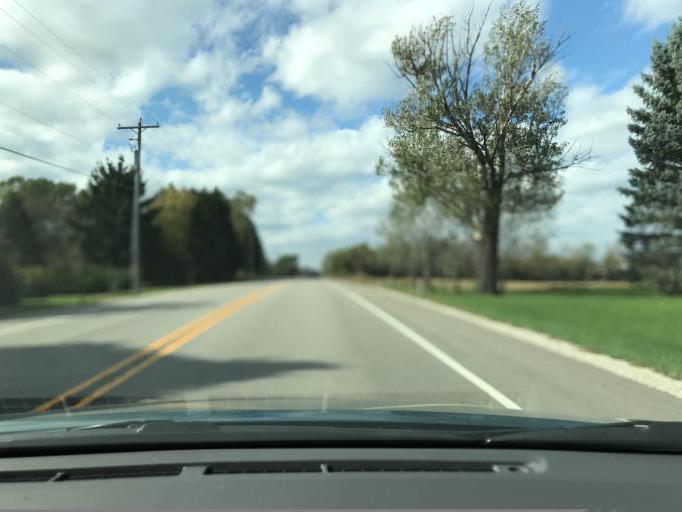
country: US
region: Wisconsin
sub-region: Racine County
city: Browns Lake
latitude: 42.6526
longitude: -88.2145
